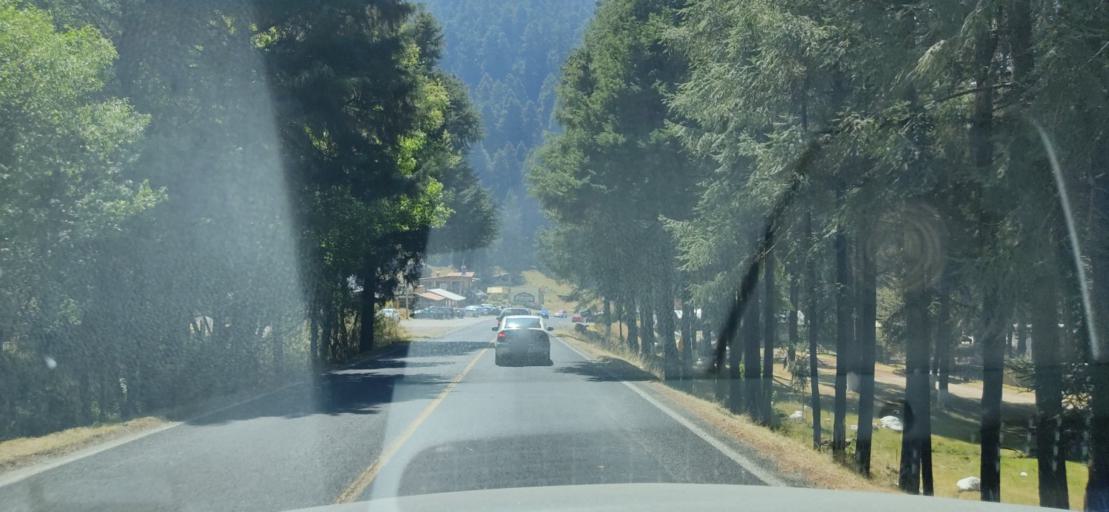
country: MX
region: Mexico
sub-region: Ocoyoacac
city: San Jeronimo Acazulco
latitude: 19.2425
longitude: -99.3751
